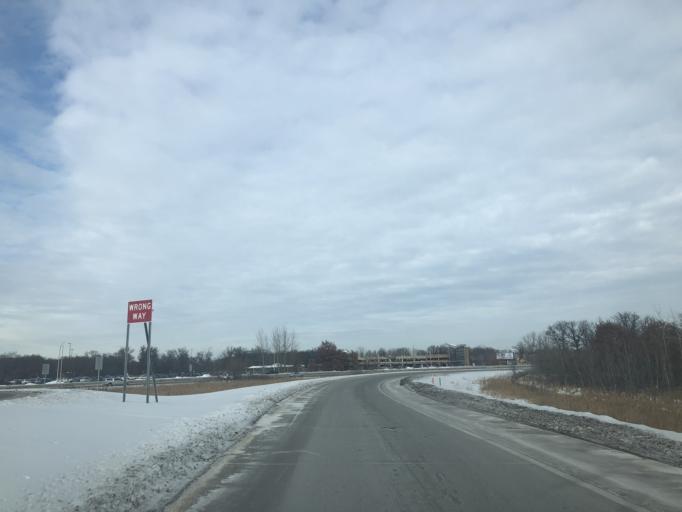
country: US
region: Minnesota
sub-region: Anoka County
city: Lexington
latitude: 45.1433
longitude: -93.1825
